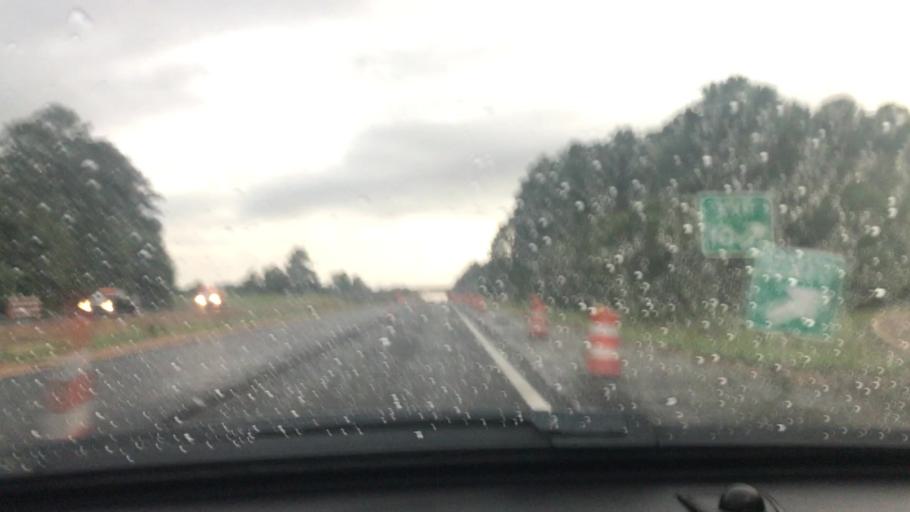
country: US
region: Mississippi
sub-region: Pike County
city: Magnolia
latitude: 31.1498
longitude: -90.4794
